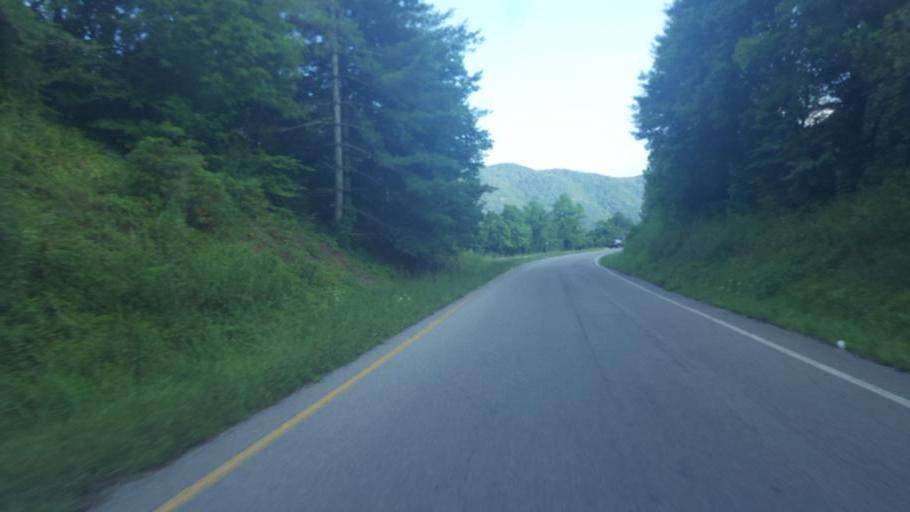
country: US
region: Virginia
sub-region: Wise County
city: Big Stone Gap
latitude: 36.8602
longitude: -82.7547
